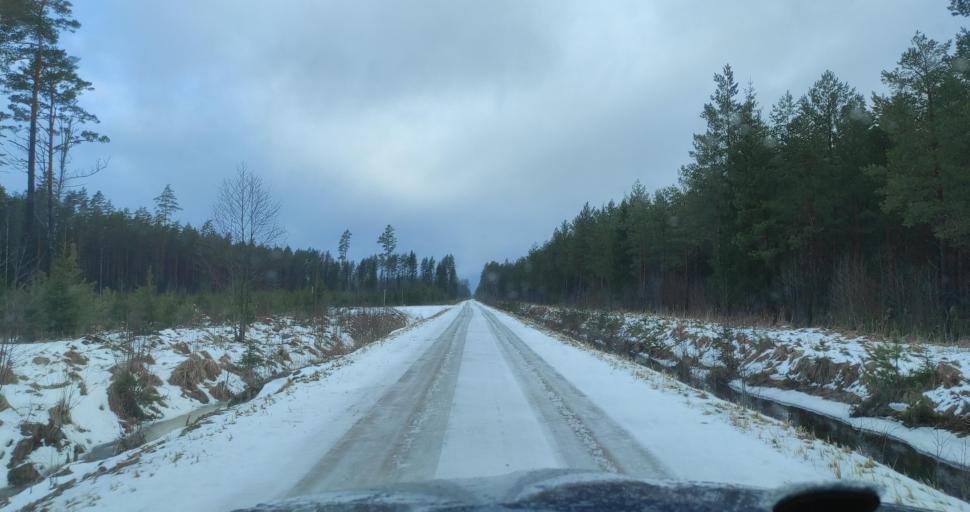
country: LV
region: Dundaga
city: Dundaga
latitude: 57.4000
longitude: 22.1087
